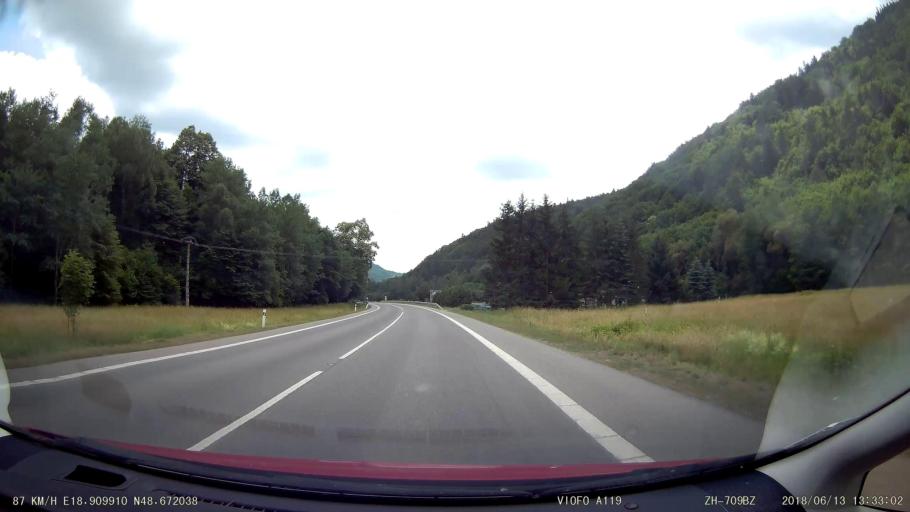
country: SK
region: Banskobystricky
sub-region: Okres Ziar nad Hronom
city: Kremnica
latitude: 48.6719
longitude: 18.9098
